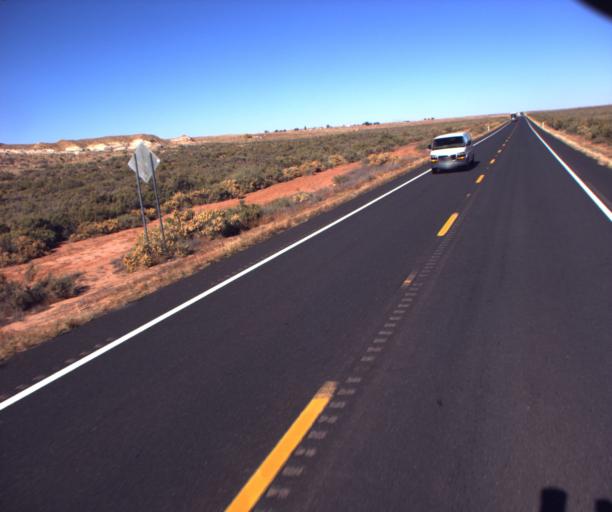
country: US
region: Arizona
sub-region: Coconino County
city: Kaibito
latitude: 36.3352
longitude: -110.9214
